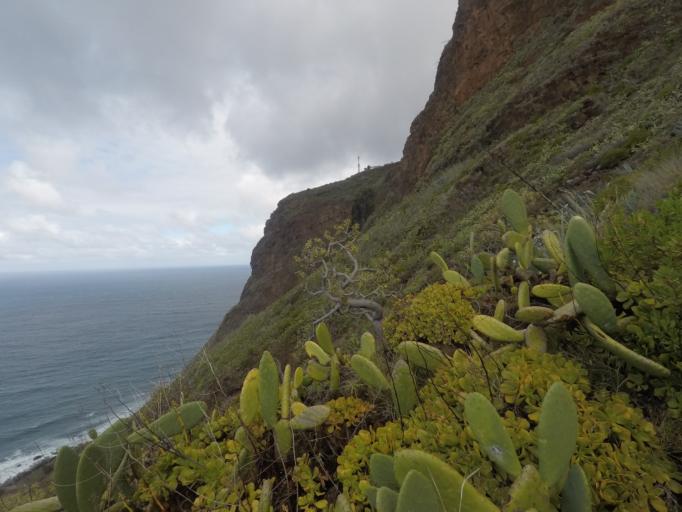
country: PT
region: Madeira
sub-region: Calheta
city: Faja da Ovelha
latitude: 32.7682
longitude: -17.2357
